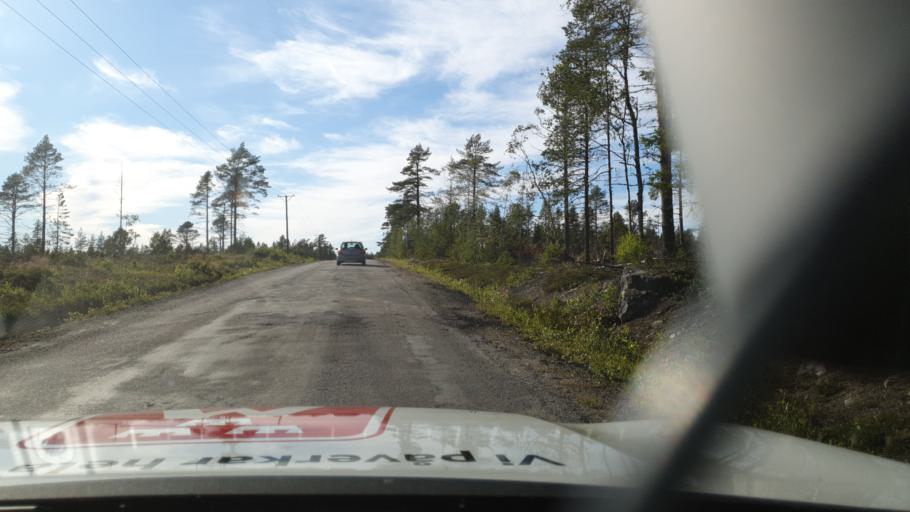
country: SE
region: Vaesterbotten
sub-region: Umea Kommun
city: Saevar
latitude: 63.8729
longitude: 20.7102
